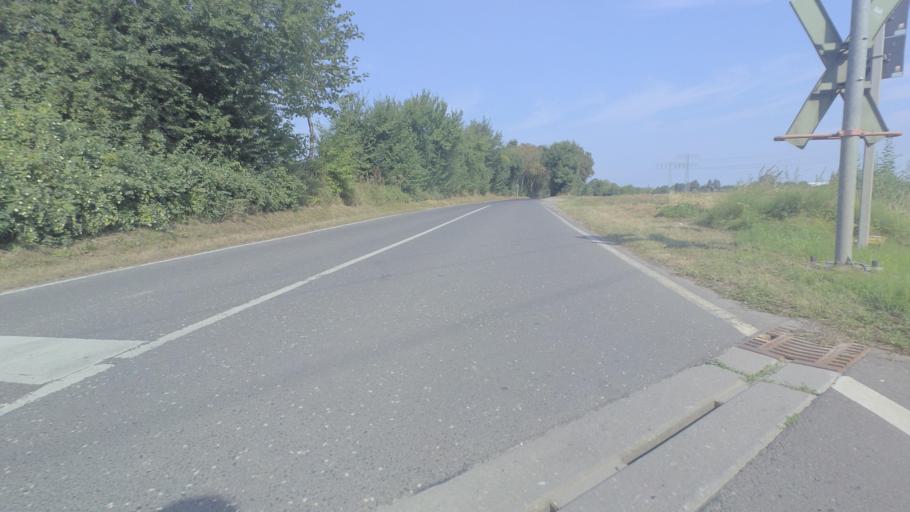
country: DE
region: Mecklenburg-Vorpommern
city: Wendorf
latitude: 54.2778
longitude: 13.0901
